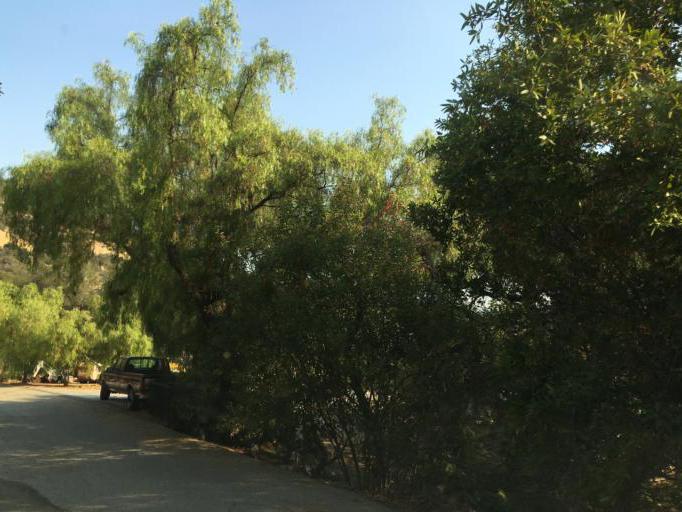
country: US
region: California
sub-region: Los Angeles County
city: Topanga
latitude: 34.0783
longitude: -118.6055
